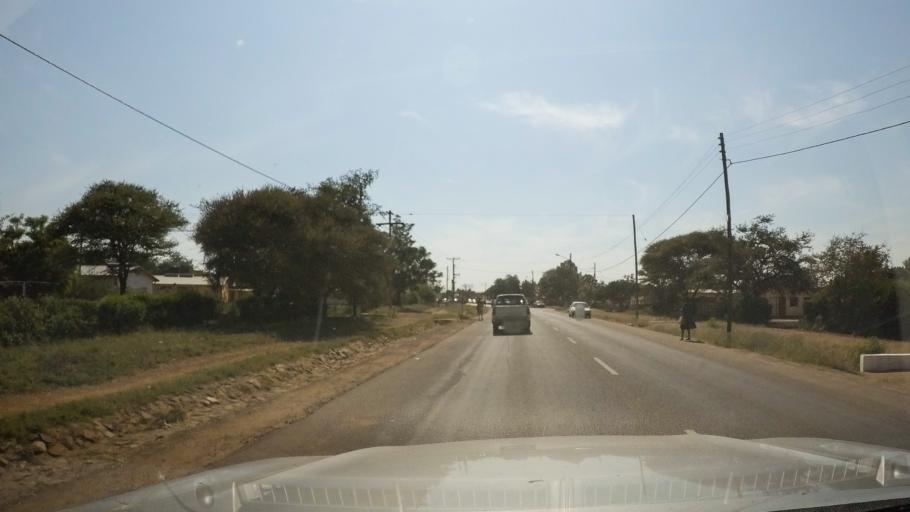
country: BW
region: South East
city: Lobatse
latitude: -25.2067
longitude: 25.6843
